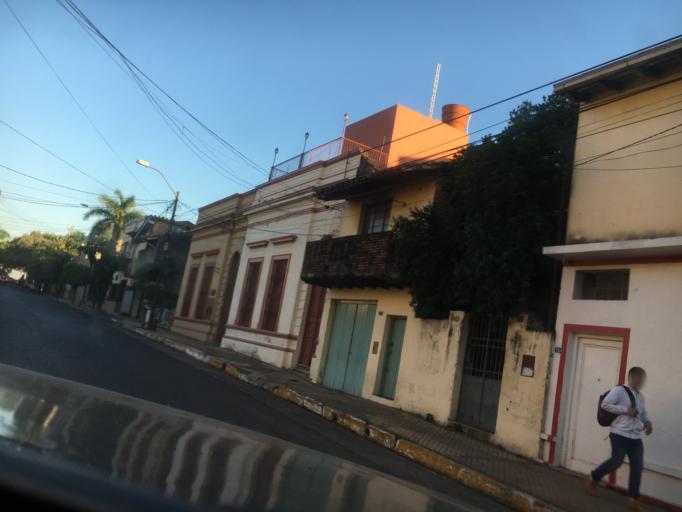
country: PY
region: Asuncion
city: Asuncion
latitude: -25.2850
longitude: -57.6441
